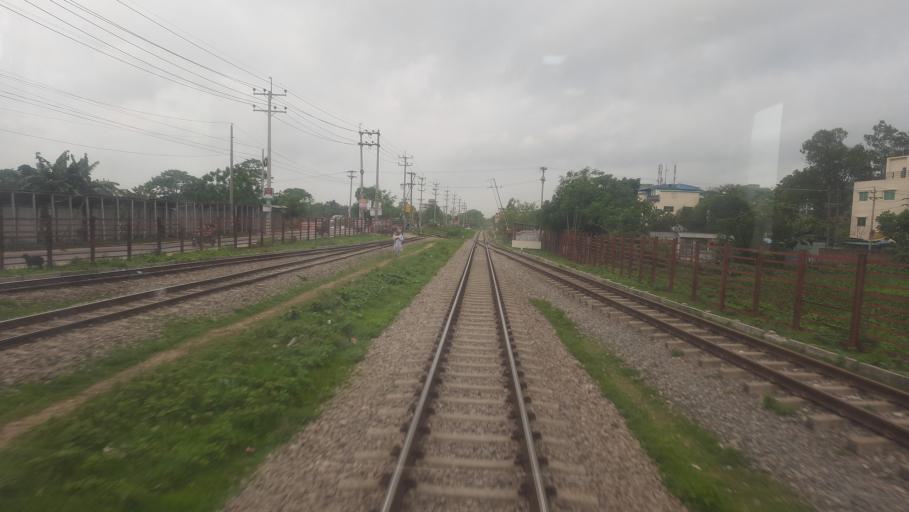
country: BD
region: Dhaka
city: Narsingdi
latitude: 23.9310
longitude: 90.7169
